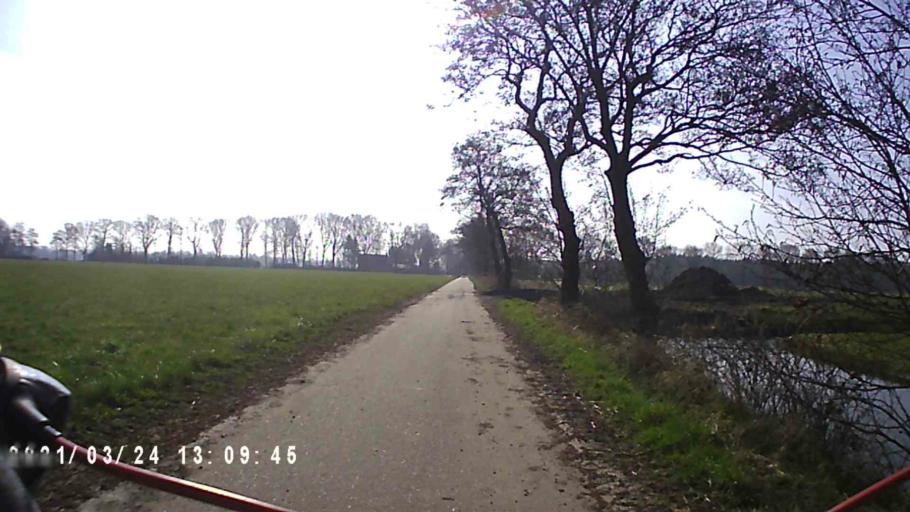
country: NL
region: Groningen
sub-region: Gemeente Leek
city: Leek
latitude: 53.1228
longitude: 6.3050
